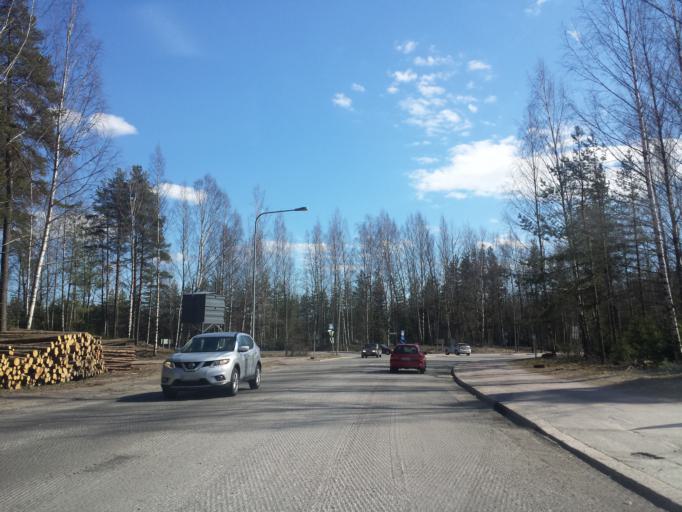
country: FI
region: Uusimaa
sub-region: Helsinki
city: Vantaa
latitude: 60.2609
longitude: 25.0839
